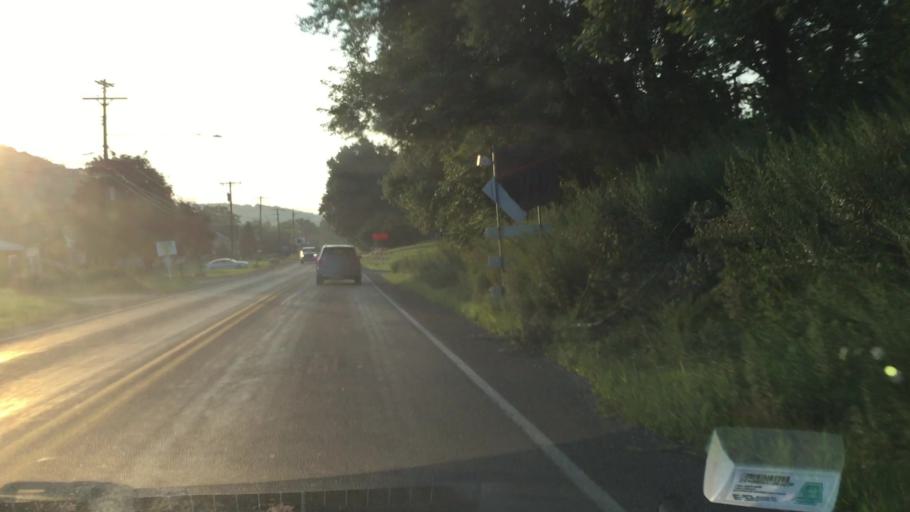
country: US
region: Pennsylvania
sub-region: Butler County
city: Evans City
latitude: 40.7629
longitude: -80.0521
